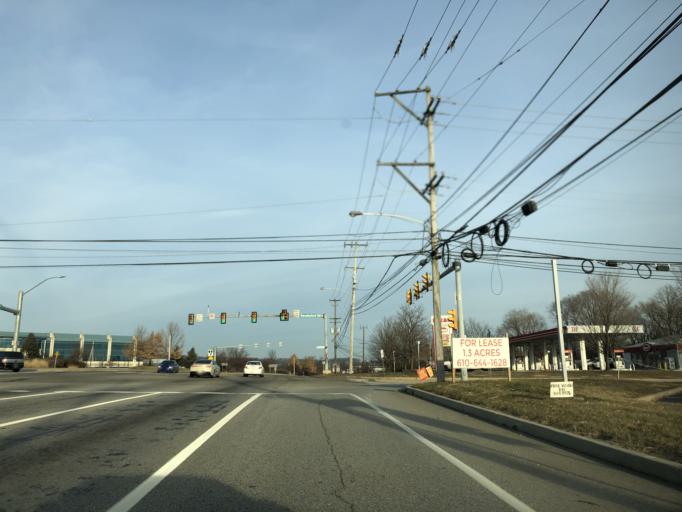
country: US
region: Pennsylvania
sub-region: Chester County
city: Malvern
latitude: 40.0521
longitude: -75.5270
